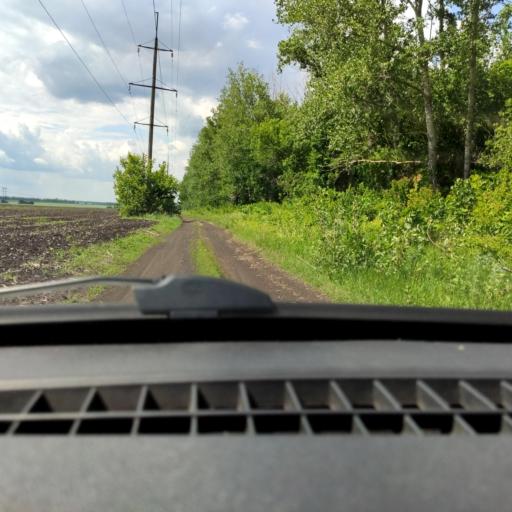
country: RU
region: Bashkortostan
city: Kabakovo
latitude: 54.5048
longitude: 56.1239
